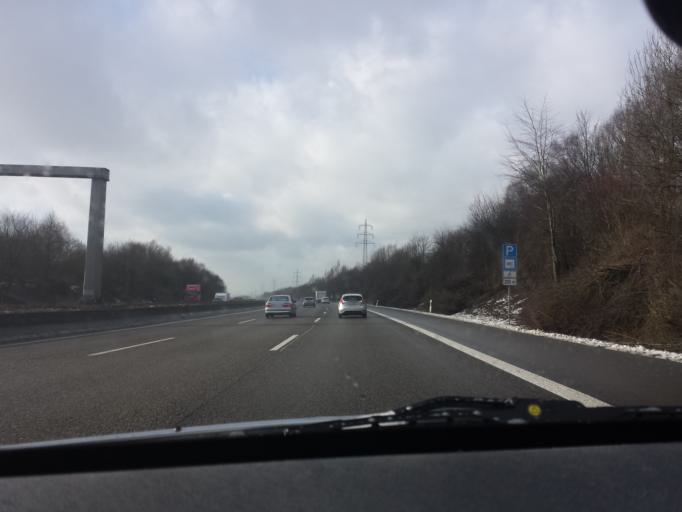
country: DE
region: North Rhine-Westphalia
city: Haan
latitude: 51.2076
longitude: 7.0249
